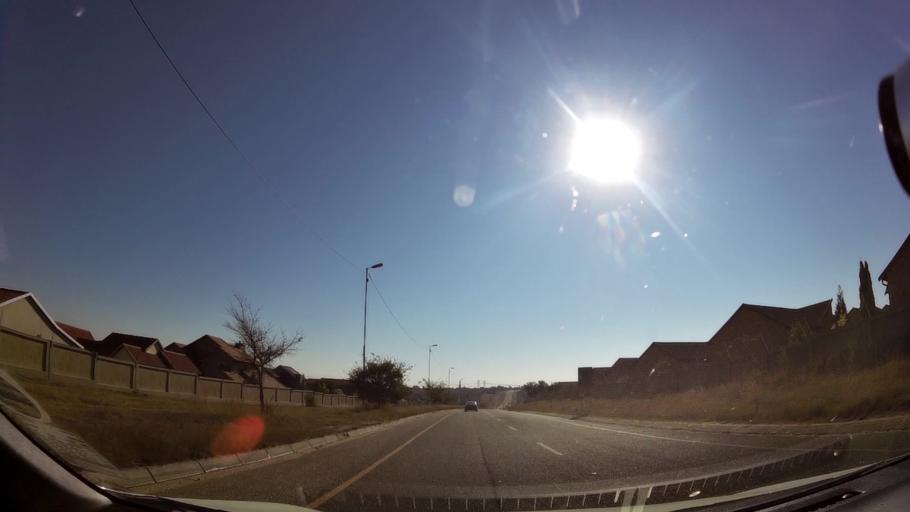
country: ZA
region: Gauteng
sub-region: City of Johannesburg Metropolitan Municipality
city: Midrand
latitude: -25.9194
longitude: 28.1326
